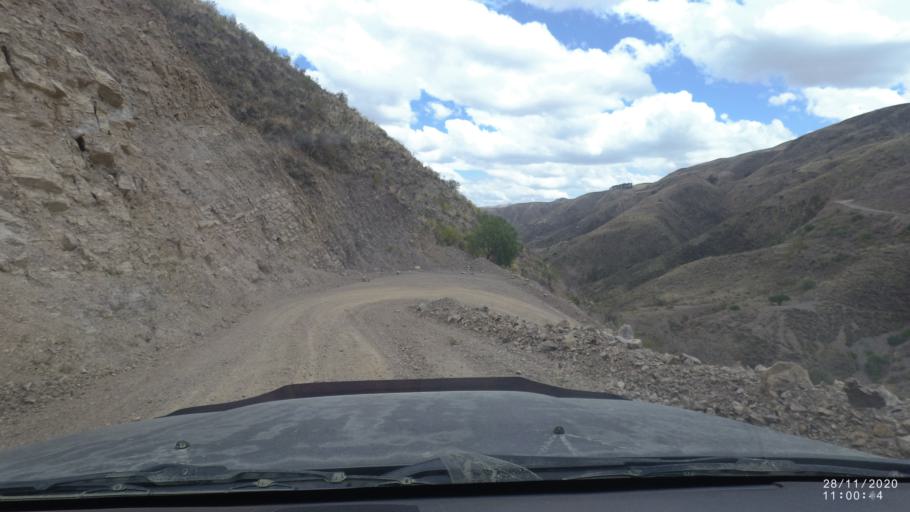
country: BO
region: Cochabamba
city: Capinota
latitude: -17.7676
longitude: -66.1060
